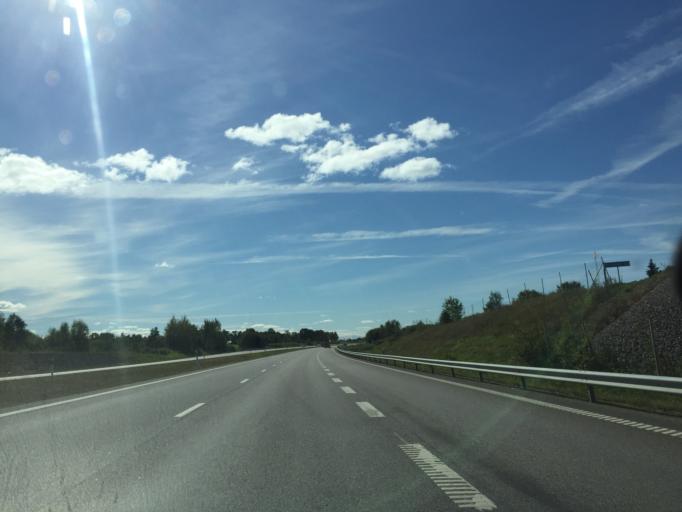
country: SE
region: OErebro
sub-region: Lindesbergs Kommun
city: Fellingsbro
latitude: 59.3356
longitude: 15.5334
